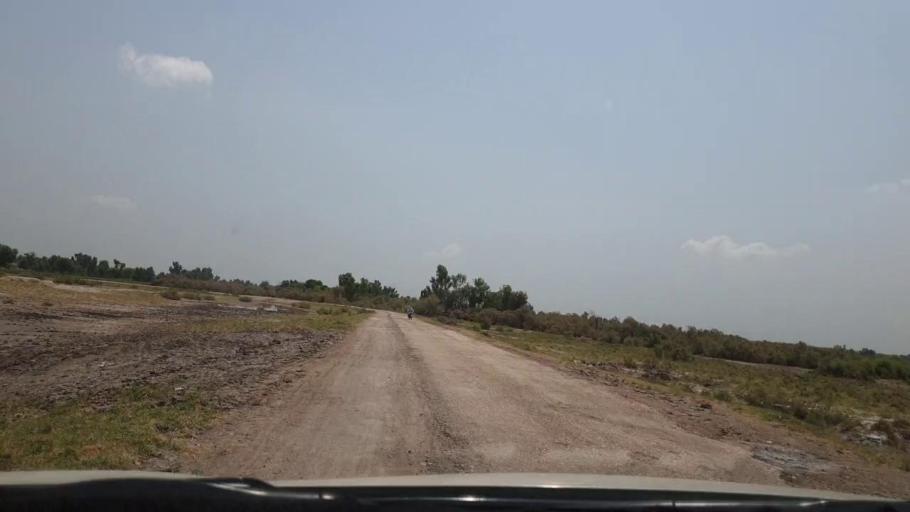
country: PK
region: Sindh
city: New Badah
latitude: 27.2985
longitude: 68.0652
